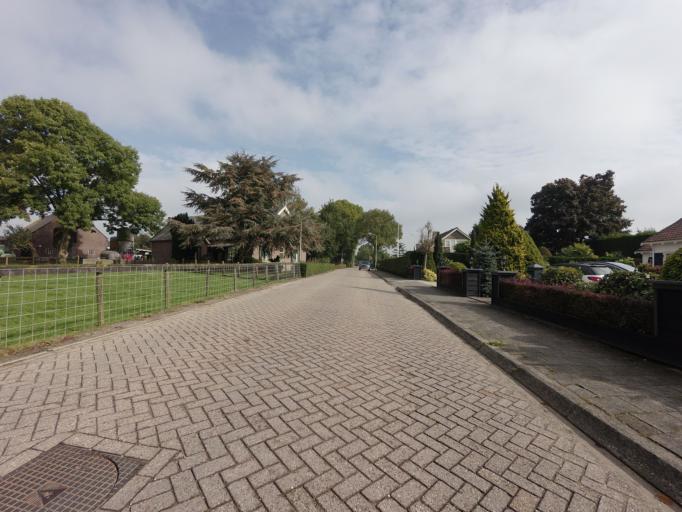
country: NL
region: Utrecht
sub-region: Gemeente Lopik
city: Lopik
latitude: 51.9543
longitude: 4.9580
